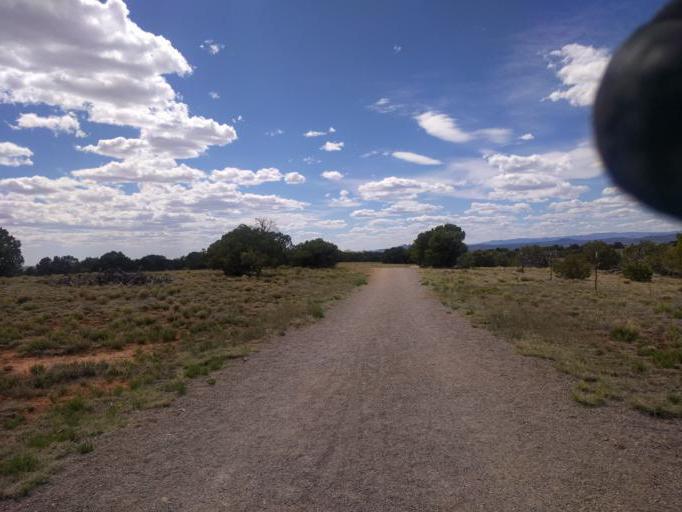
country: US
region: New Mexico
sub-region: Santa Fe County
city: Agua Fria
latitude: 35.5990
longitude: -105.9978
